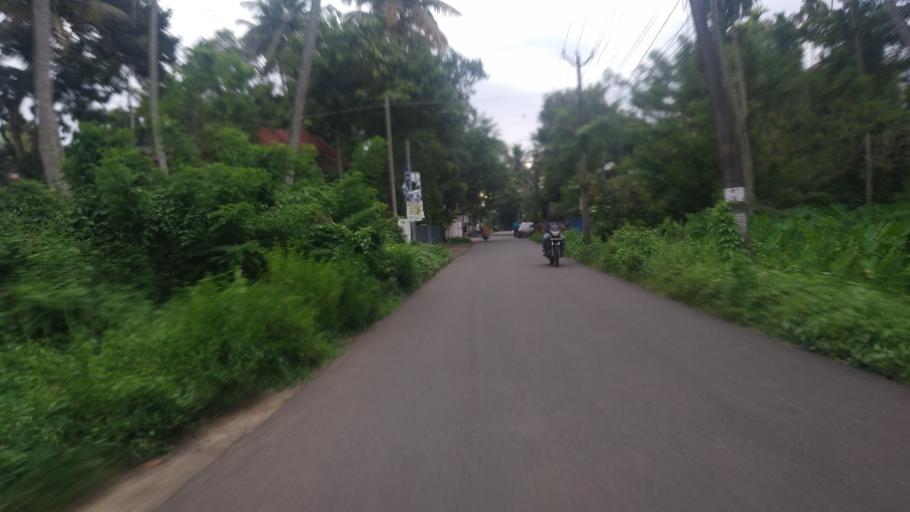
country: IN
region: Kerala
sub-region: Alappuzha
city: Arukutti
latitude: 9.8611
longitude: 76.2897
